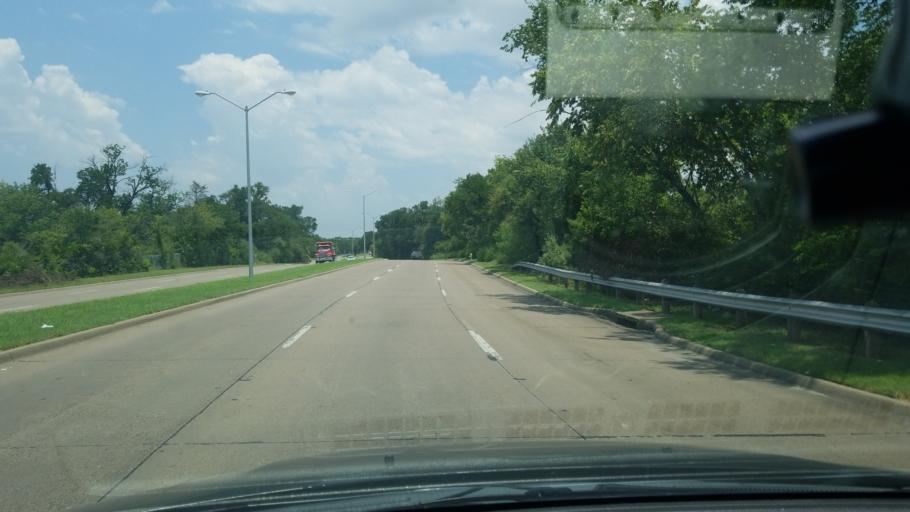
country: US
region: Texas
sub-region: Dallas County
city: Balch Springs
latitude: 32.7206
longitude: -96.6656
